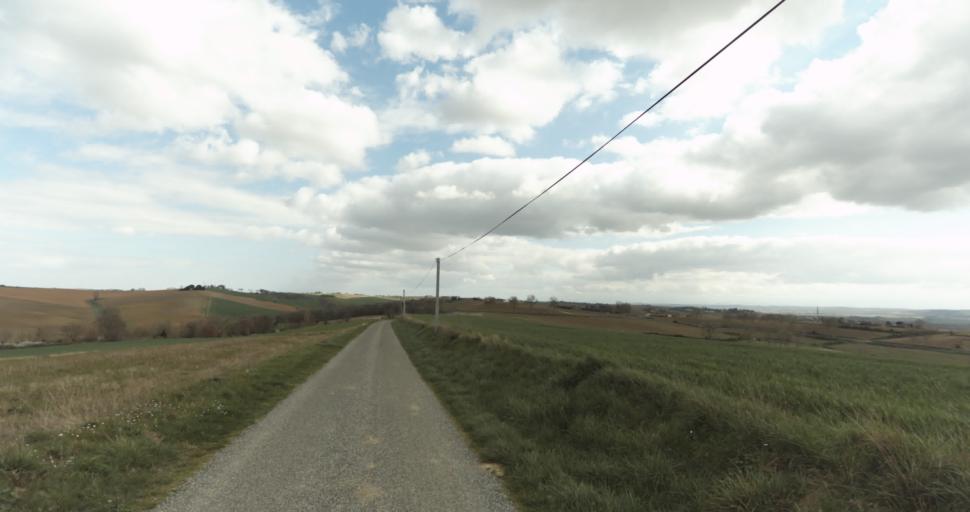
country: FR
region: Midi-Pyrenees
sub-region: Departement de la Haute-Garonne
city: Auterive
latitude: 43.3637
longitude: 1.4928
